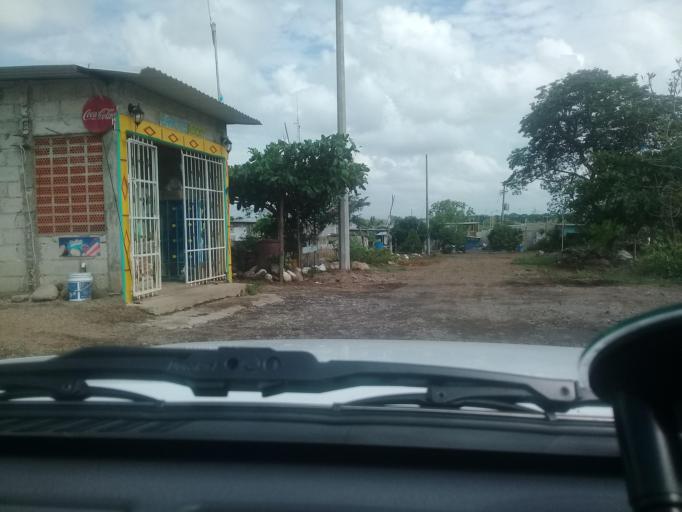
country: MX
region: Veracruz
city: Paso de Ovejas
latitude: 19.2751
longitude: -96.4212
